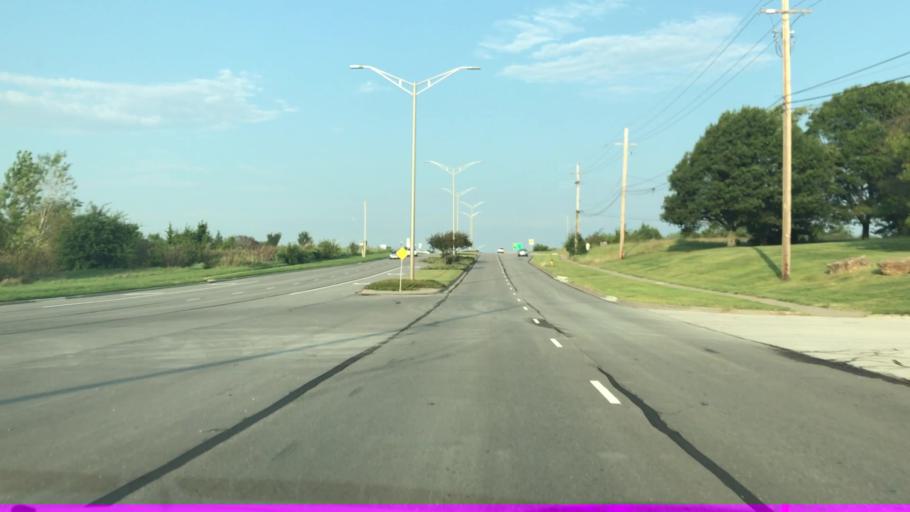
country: US
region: Kansas
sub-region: Johnson County
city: Olathe
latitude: 38.9273
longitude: -94.8484
